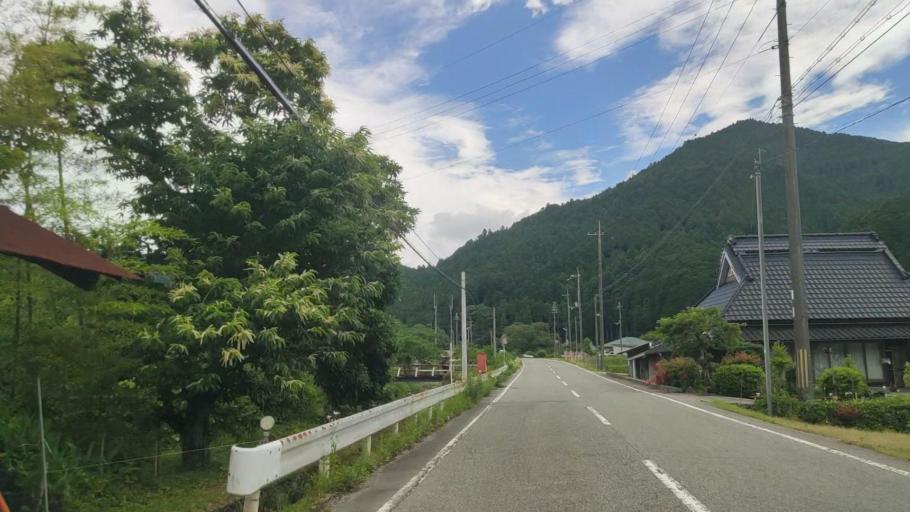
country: JP
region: Kyoto
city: Fukuchiyama
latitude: 35.1998
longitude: 134.9367
